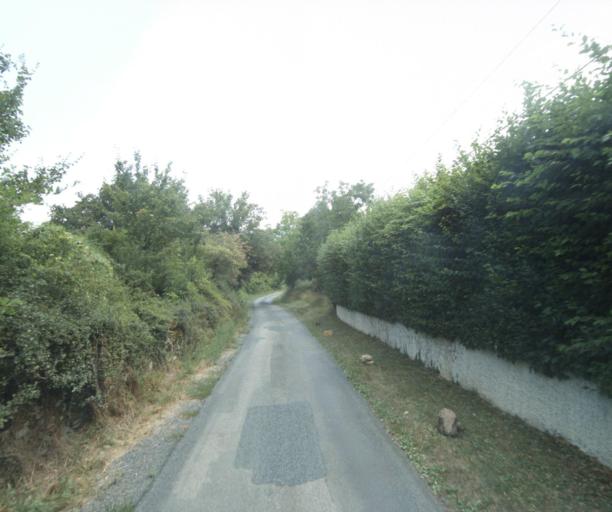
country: FR
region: Rhone-Alpes
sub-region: Departement du Rhone
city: Saint-Germain-Nuelles
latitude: 45.8451
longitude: 4.5988
